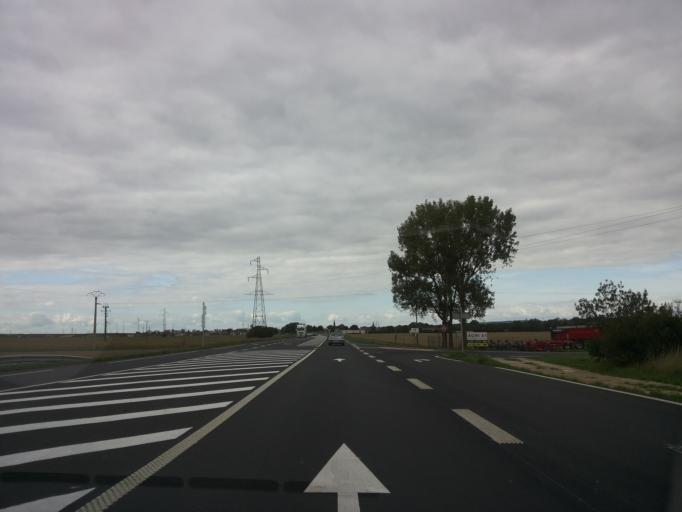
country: FR
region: Champagne-Ardenne
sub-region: Departement de la Marne
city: Verzy
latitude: 49.1641
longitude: 4.1969
